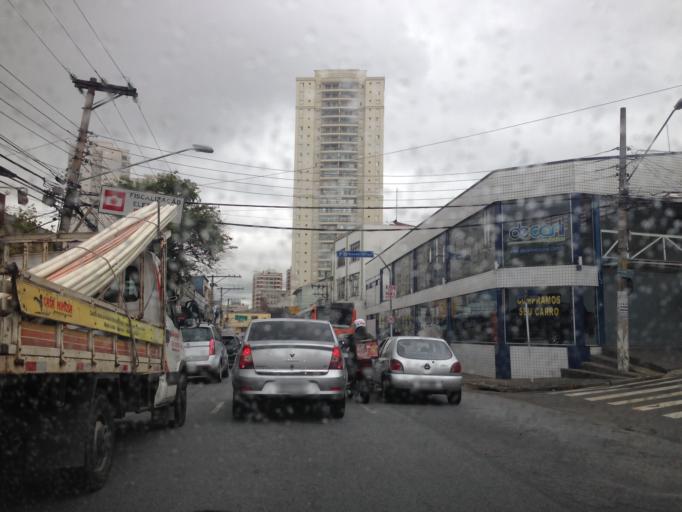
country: BR
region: Sao Paulo
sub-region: Sao Paulo
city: Sao Paulo
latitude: -23.5272
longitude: -46.7023
